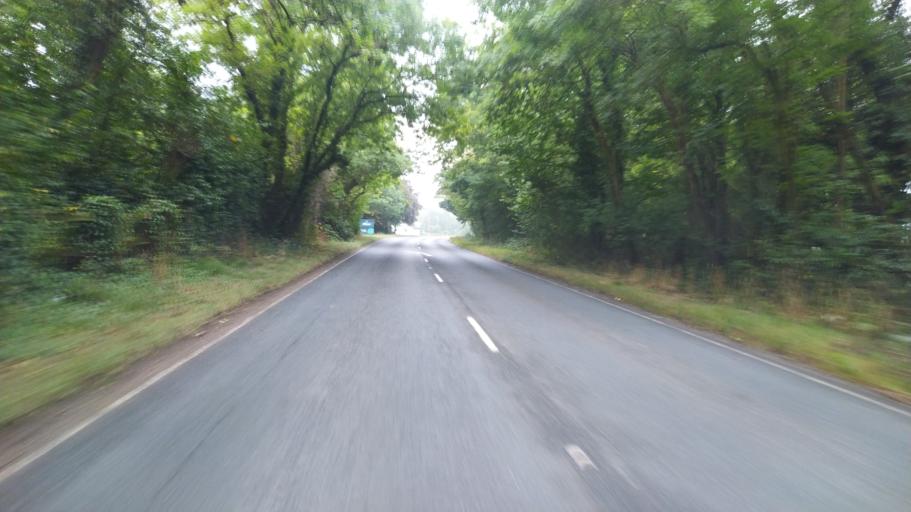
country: GB
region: England
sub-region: Hampshire
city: New Milton
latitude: 50.7734
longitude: -1.6964
